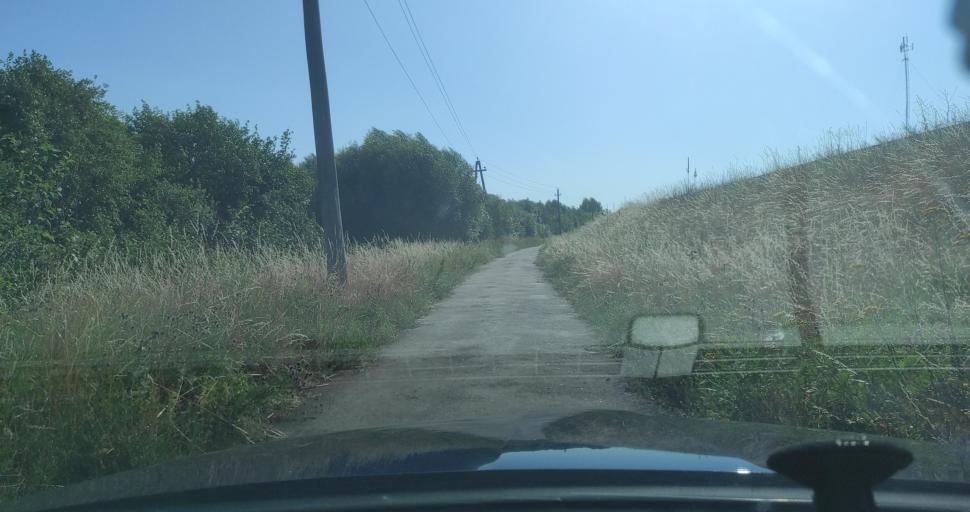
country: LV
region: Skrunda
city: Skrunda
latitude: 56.6813
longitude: 22.0302
